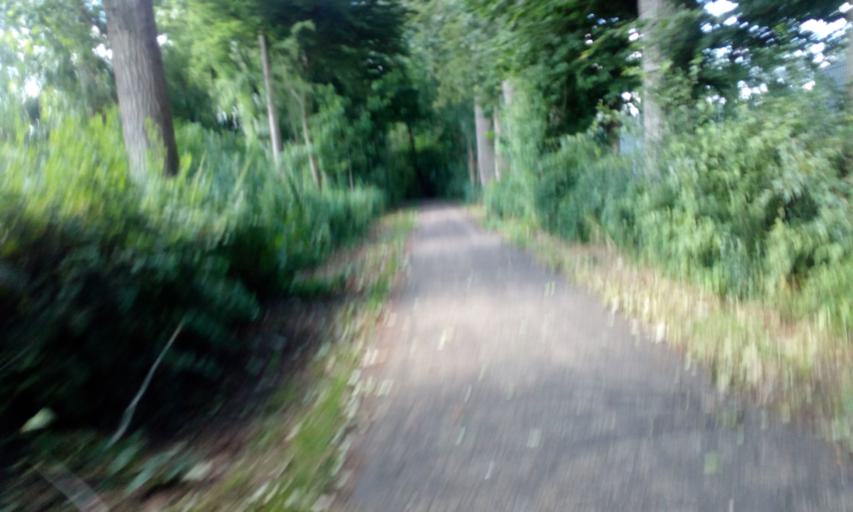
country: NL
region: South Holland
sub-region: Gemeente Lansingerland
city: Berkel en Rodenrijs
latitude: 51.9653
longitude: 4.4813
